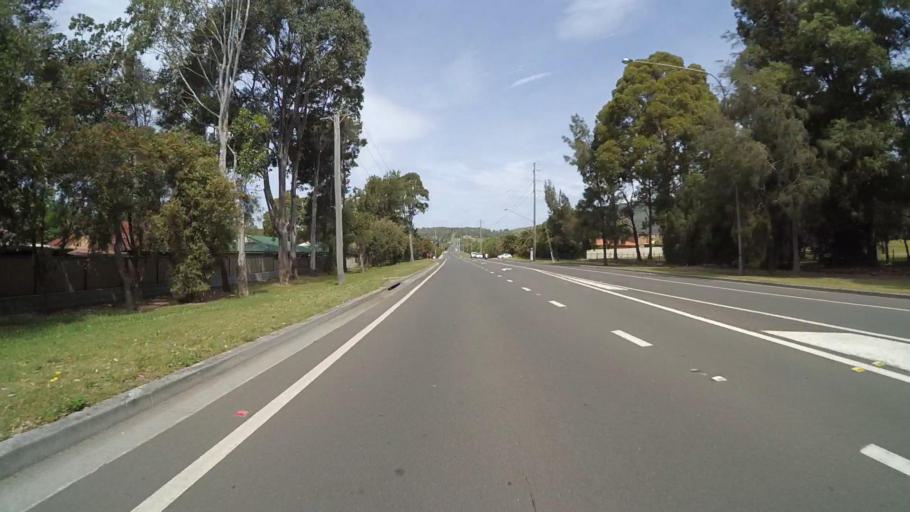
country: AU
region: New South Wales
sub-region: Shellharbour
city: Albion Park Rail
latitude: -34.5826
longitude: 150.7784
